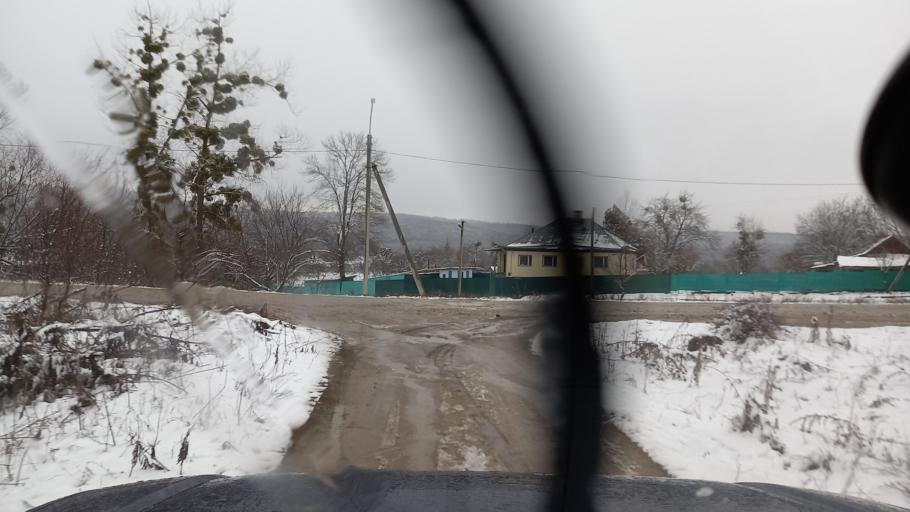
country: RU
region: Adygeya
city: Abadzekhskaya
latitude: 44.3520
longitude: 40.4106
